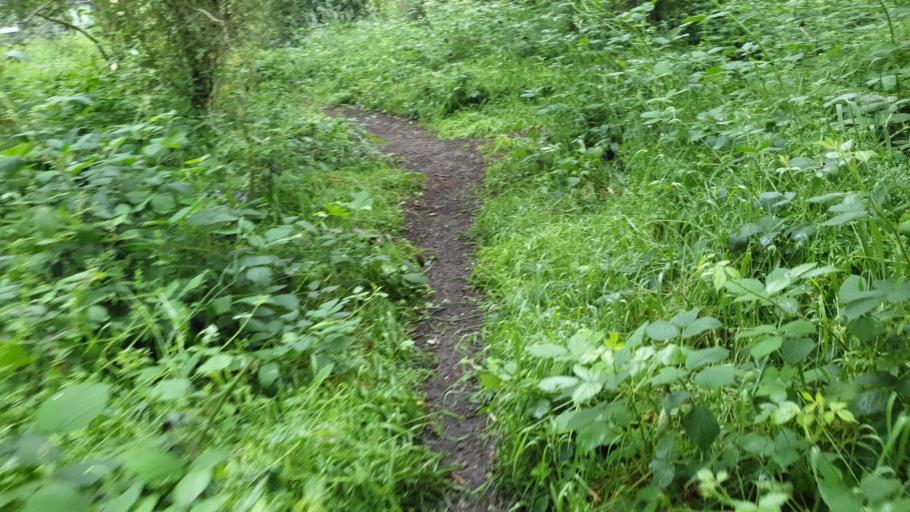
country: GB
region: England
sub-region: Essex
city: Great Bentley
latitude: 51.8851
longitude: 1.1042
